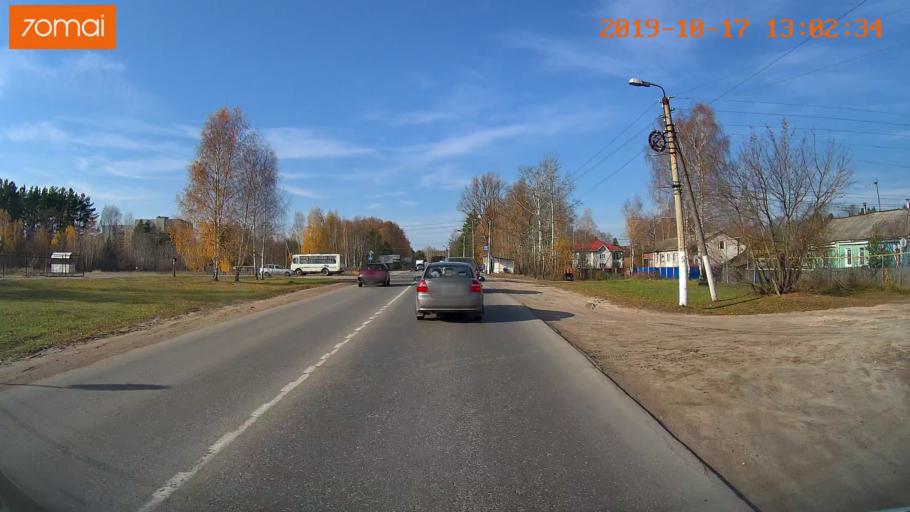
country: RU
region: Rjazan
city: Kasimov
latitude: 54.9504
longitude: 41.3609
